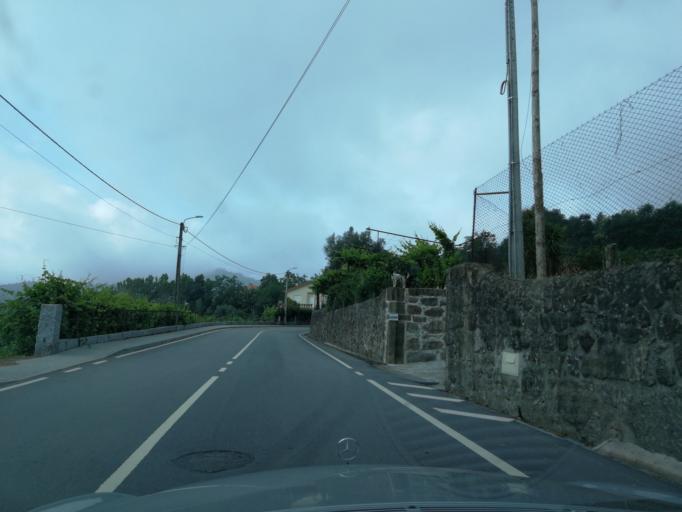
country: PT
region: Braga
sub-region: Braga
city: Braga
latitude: 41.5204
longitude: -8.3681
